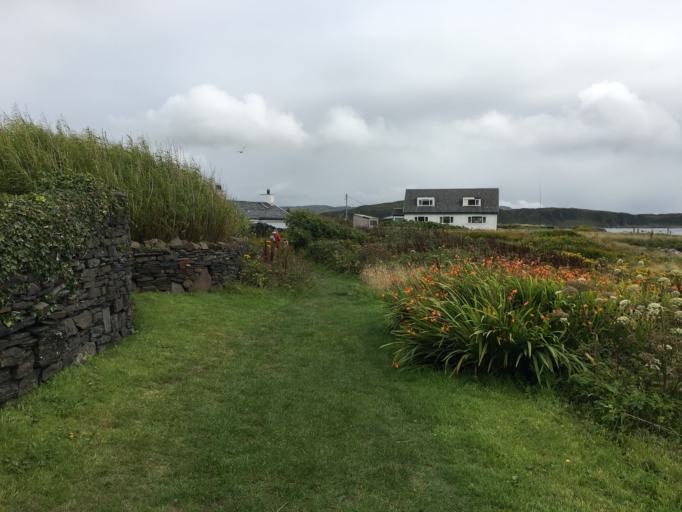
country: GB
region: Scotland
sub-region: Argyll and Bute
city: Isle Of Mull
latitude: 56.2912
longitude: -5.6572
